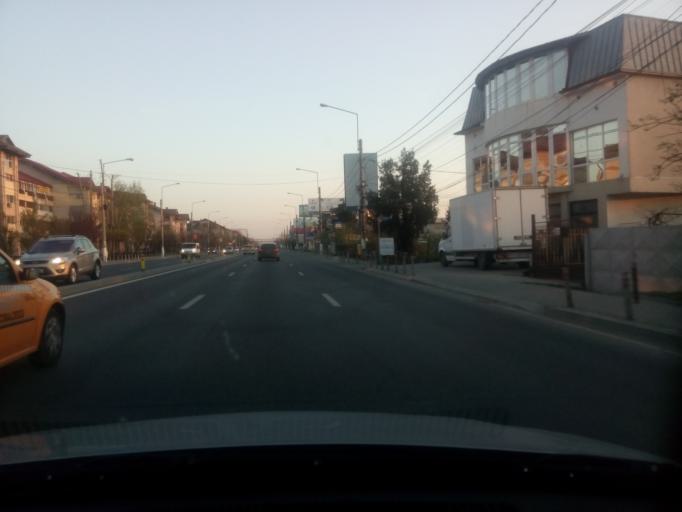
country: RO
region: Ilfov
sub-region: Comuna Otopeni
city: Otopeni
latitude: 44.5497
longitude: 26.0690
